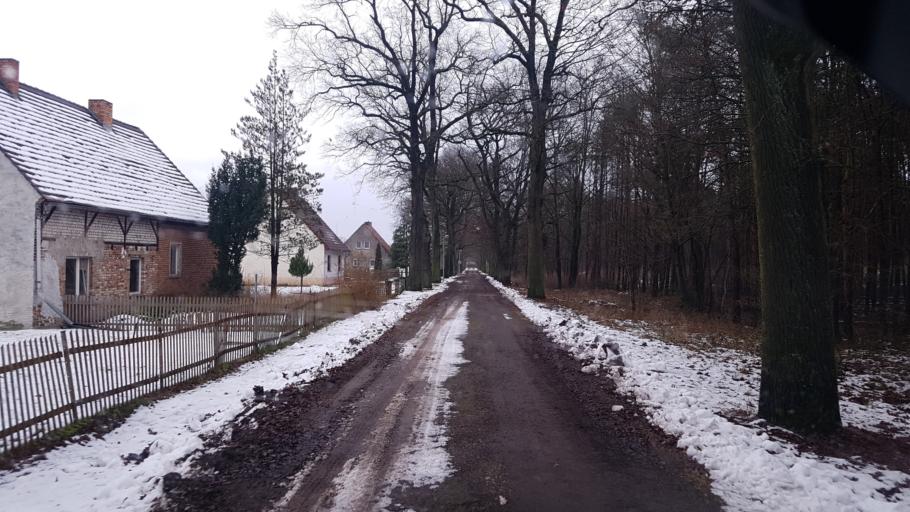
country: DE
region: Brandenburg
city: Schenkendobern
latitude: 51.9677
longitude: 14.5768
